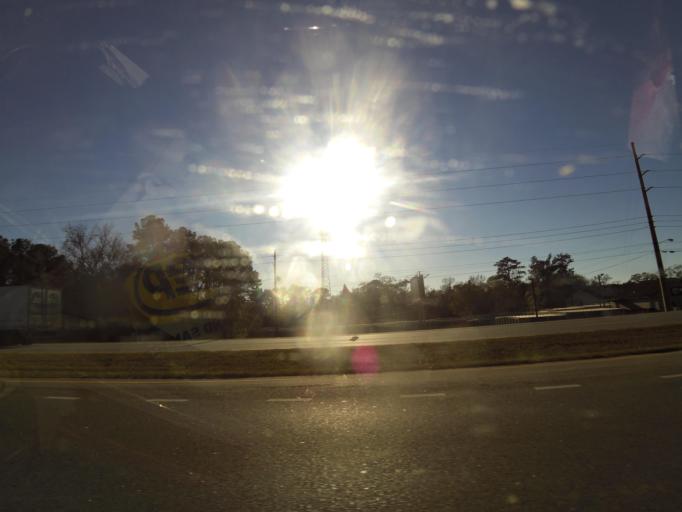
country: US
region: Alabama
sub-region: Houston County
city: Dothan
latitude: 31.2096
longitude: -85.4260
